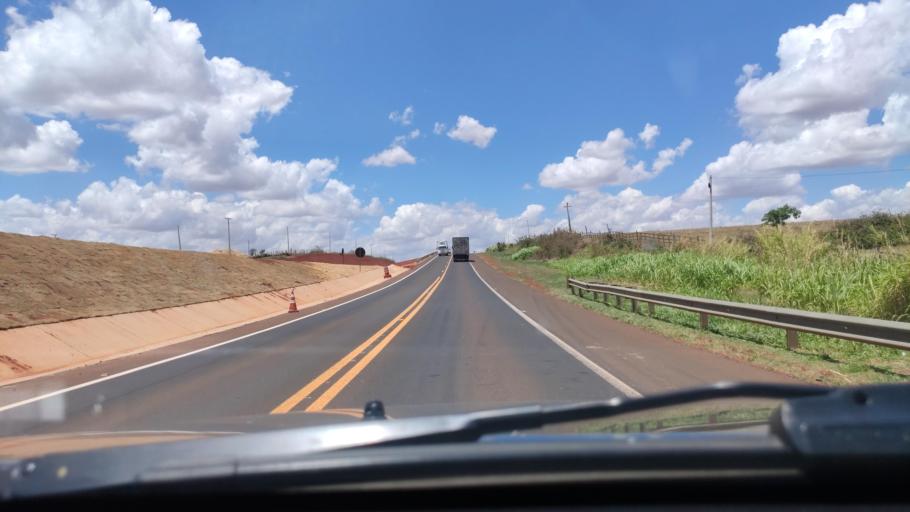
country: BR
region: Sao Paulo
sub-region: Jau
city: Jau
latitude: -22.2053
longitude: -48.5138
